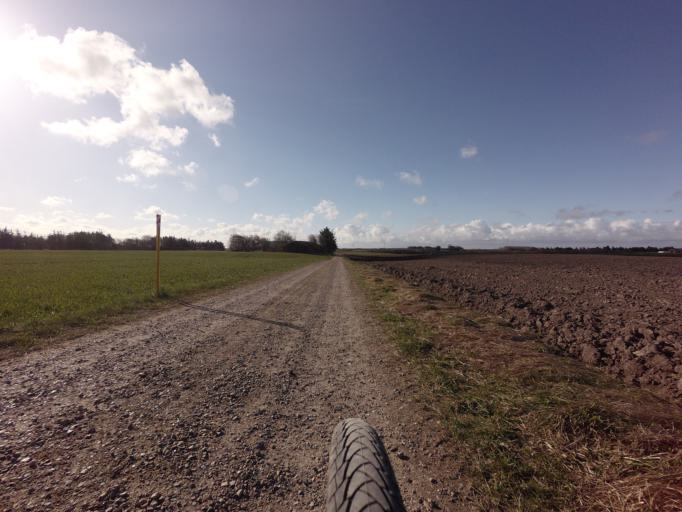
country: DK
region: North Denmark
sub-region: Hjorring Kommune
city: Vra
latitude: 57.3621
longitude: 9.8168
